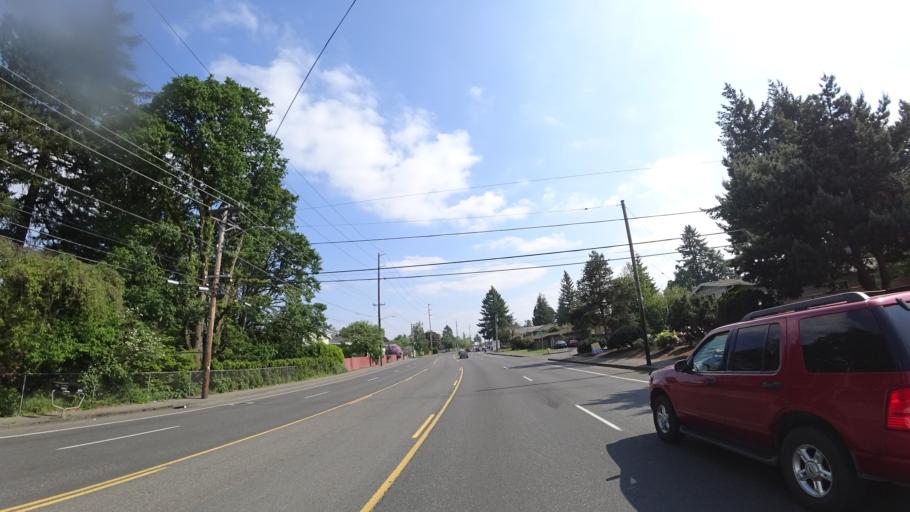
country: US
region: Oregon
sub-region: Multnomah County
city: Fairview
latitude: 45.5311
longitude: -122.4773
